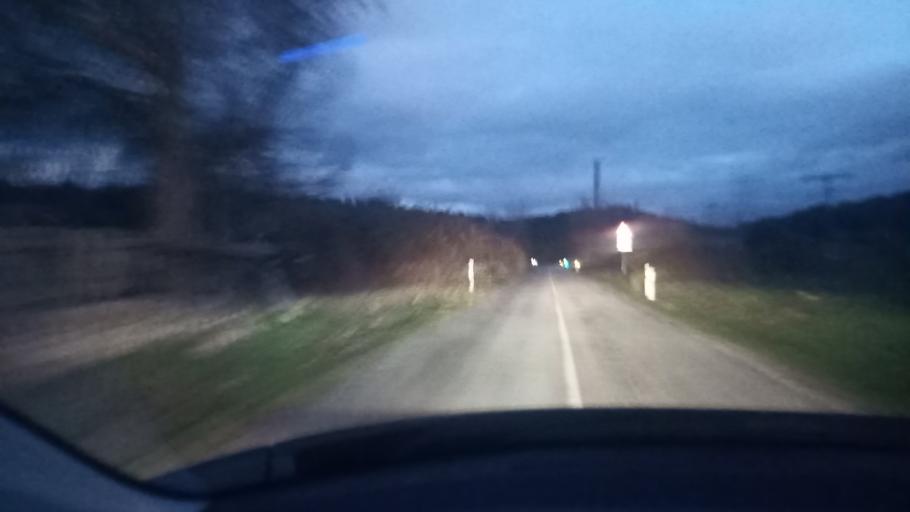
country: ES
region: Madrid
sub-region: Provincia de Madrid
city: Colmenar del Arroyo
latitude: 40.4454
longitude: -4.2279
